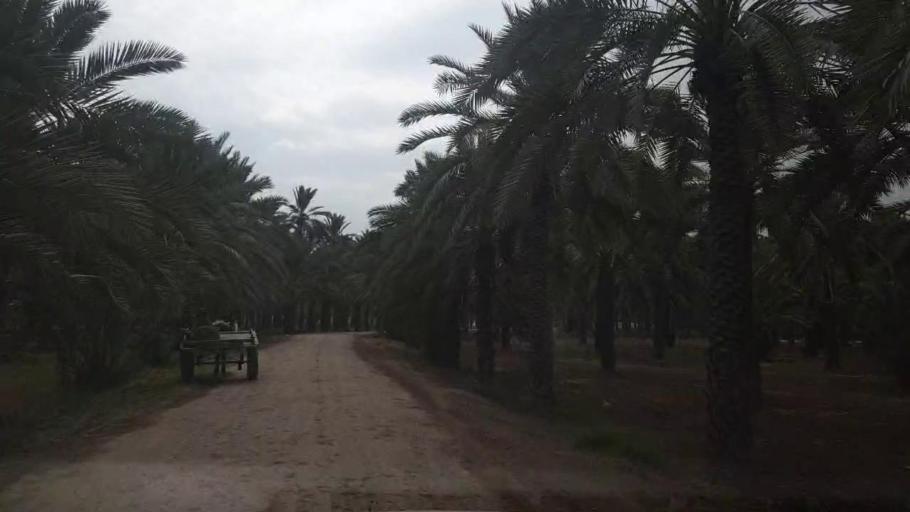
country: PK
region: Sindh
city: Khairpur
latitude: 27.6057
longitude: 68.8139
